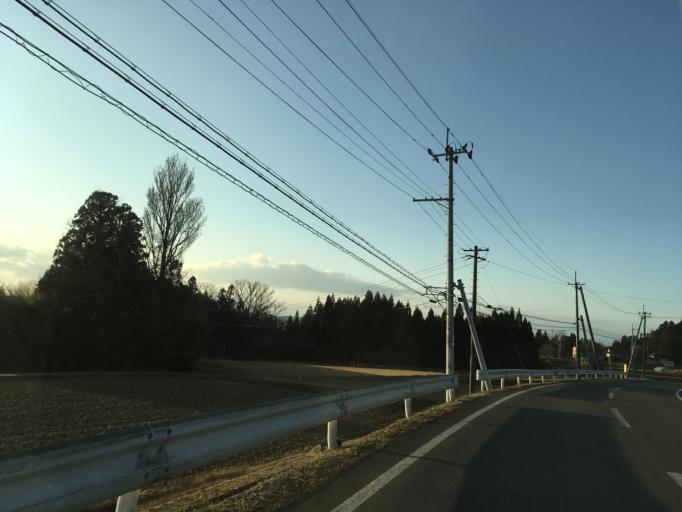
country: JP
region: Iwate
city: Ichinoseki
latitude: 38.8204
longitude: 141.2126
